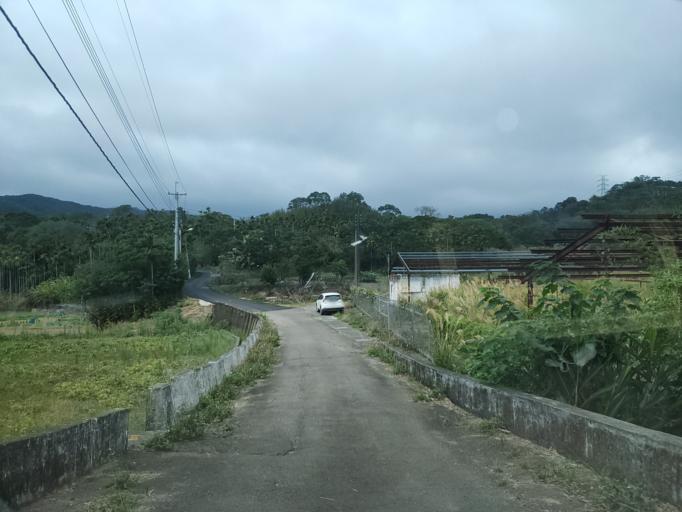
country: TW
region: Taiwan
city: Fengyuan
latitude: 24.3576
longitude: 120.7787
